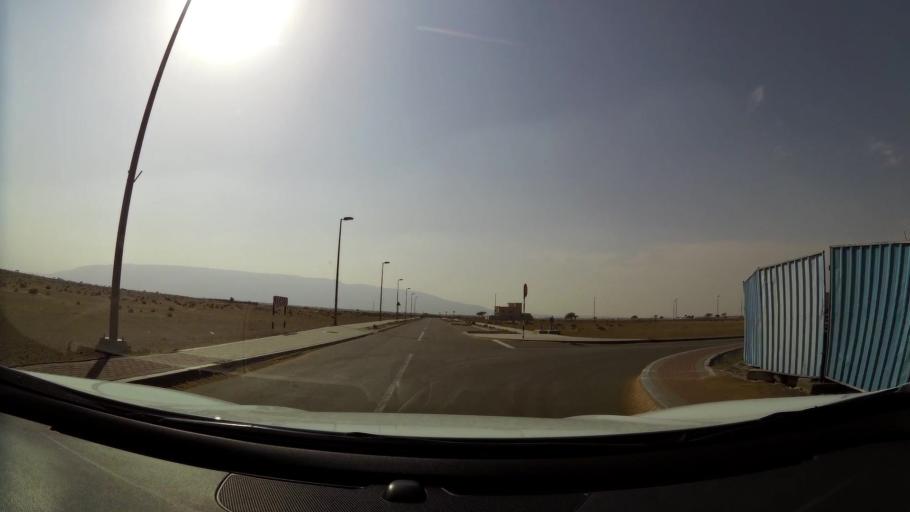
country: AE
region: Abu Dhabi
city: Al Ain
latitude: 24.0852
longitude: 55.9000
